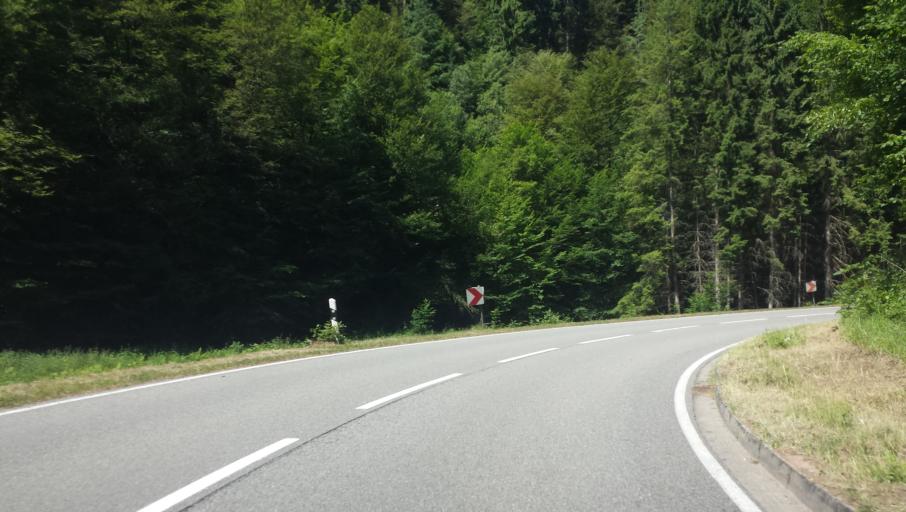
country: DE
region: Rheinland-Pfalz
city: Elmstein
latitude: 49.3594
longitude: 7.9111
